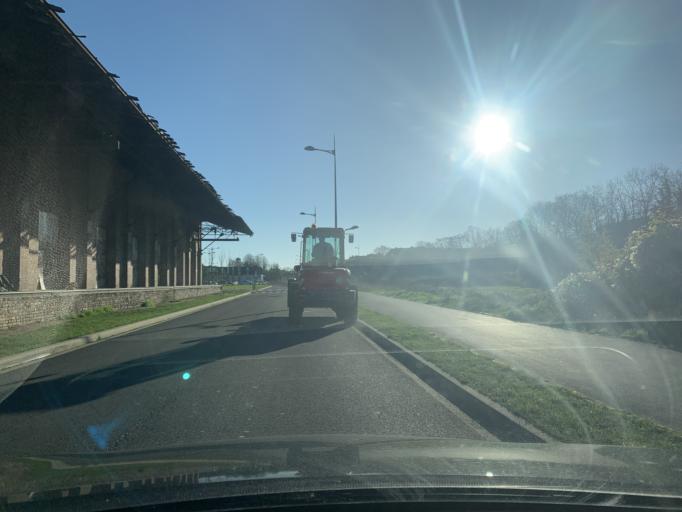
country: FR
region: Nord-Pas-de-Calais
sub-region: Departement du Nord
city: Cambrai
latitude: 50.1756
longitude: 3.2422
